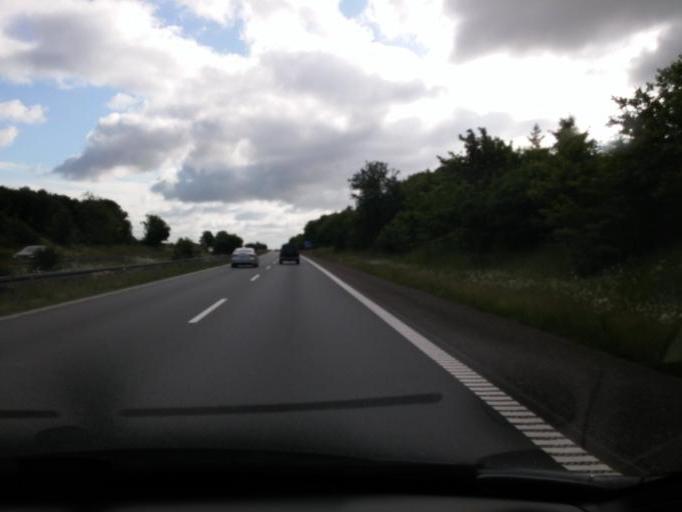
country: DK
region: Zealand
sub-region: Koge Kommune
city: Ejby
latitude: 55.4708
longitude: 12.0731
